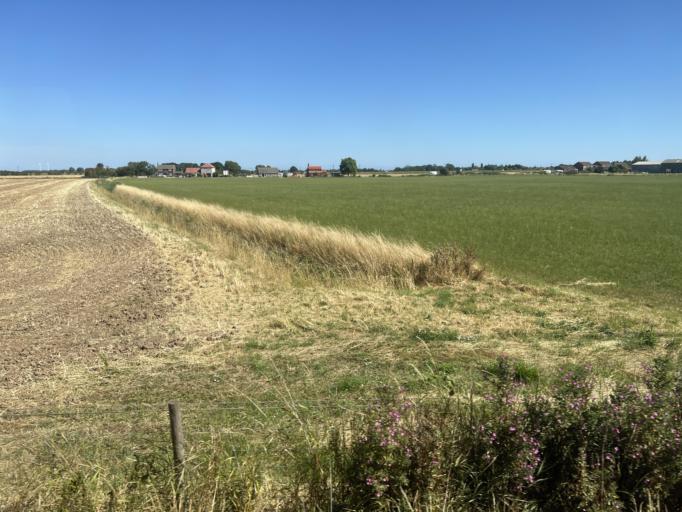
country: GB
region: England
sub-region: Lincolnshire
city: Wainfleet All Saints
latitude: 53.1096
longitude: 0.2251
